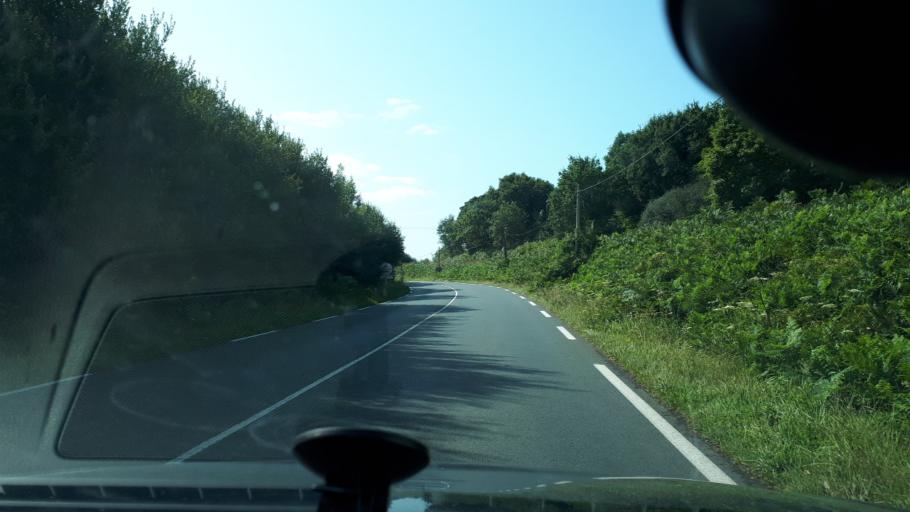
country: FR
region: Brittany
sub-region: Departement du Finistere
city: Pouldreuzic
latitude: 47.9684
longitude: -4.3701
